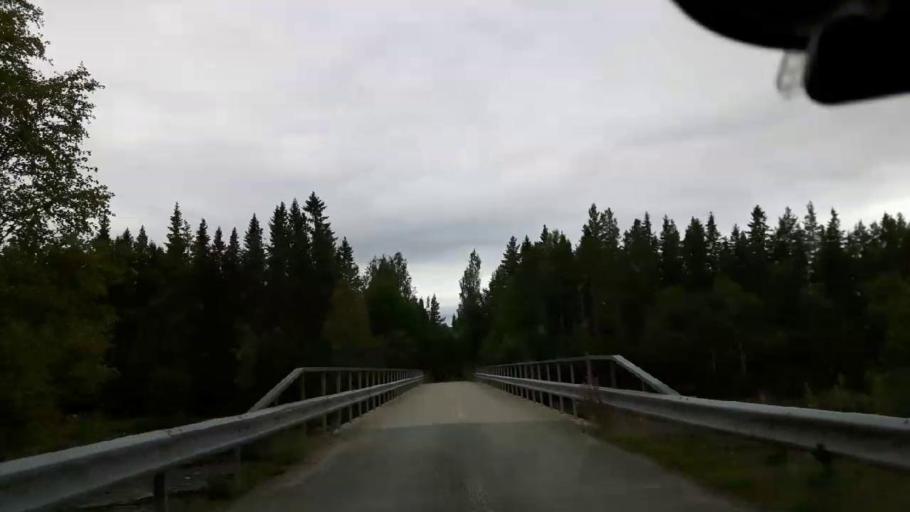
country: SE
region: Vaesternorrland
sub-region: Ange Kommun
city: Ange
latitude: 62.8183
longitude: 15.7129
